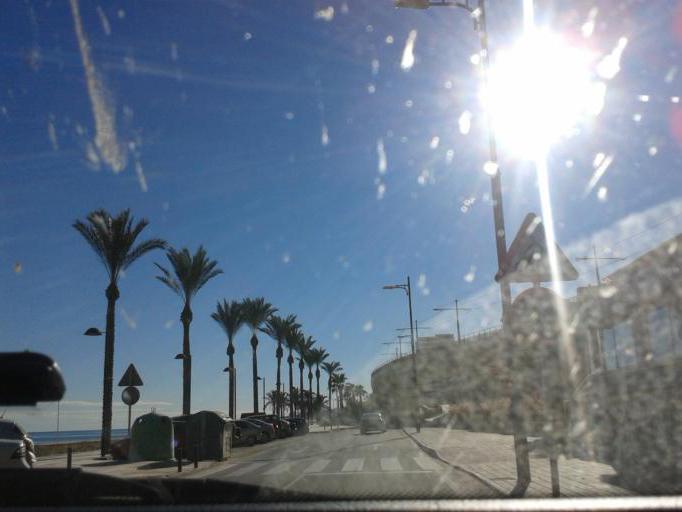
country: ES
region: Valencia
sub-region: Provincia de Alicante
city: el Campello
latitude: 38.4110
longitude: -0.4020
